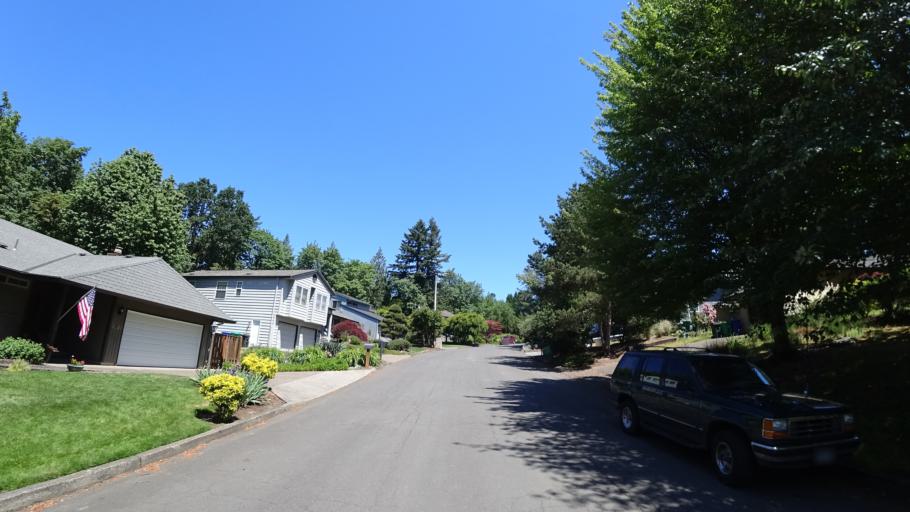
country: US
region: Oregon
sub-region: Washington County
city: Raleigh Hills
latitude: 45.4921
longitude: -122.7264
